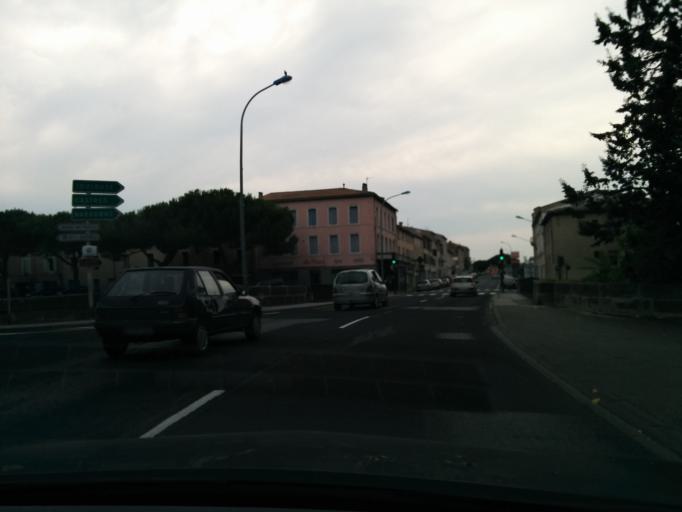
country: FR
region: Languedoc-Roussillon
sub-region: Departement de l'Aude
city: Carcassonne
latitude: 43.2166
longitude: 2.3488
